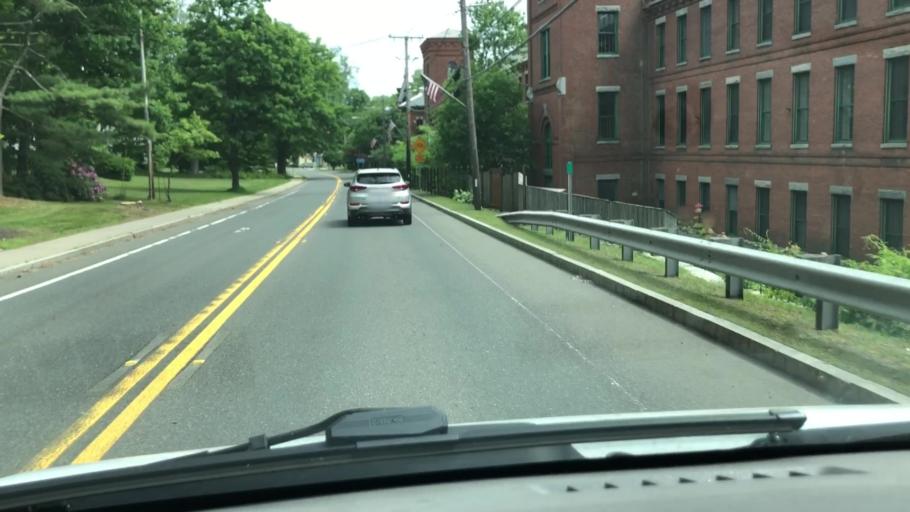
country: US
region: Massachusetts
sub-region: Hampshire County
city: Williamsburg
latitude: 42.3766
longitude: -72.7057
